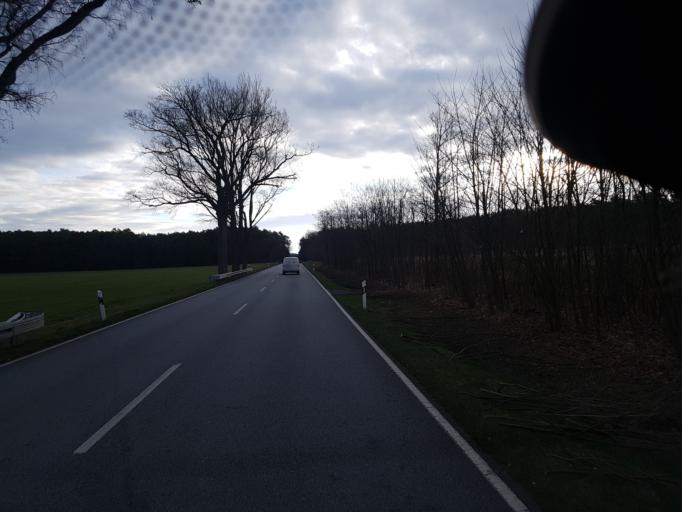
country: DE
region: Brandenburg
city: Schlepzig
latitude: 51.9903
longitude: 14.0014
